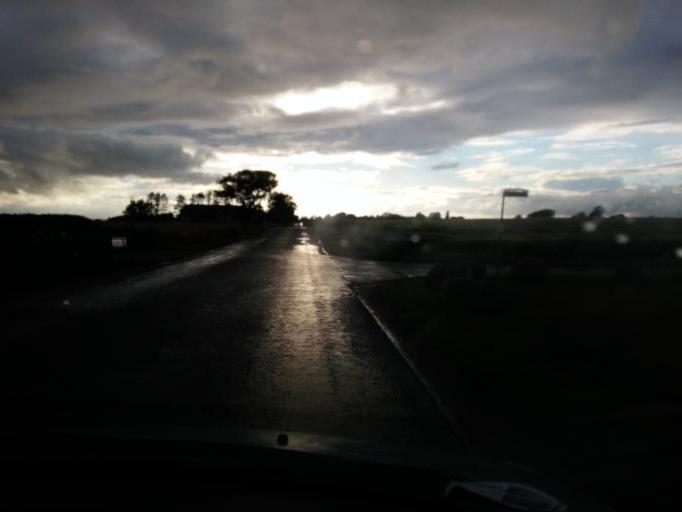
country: DK
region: South Denmark
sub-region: Kerteminde Kommune
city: Kerteminde
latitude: 55.5073
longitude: 10.6290
